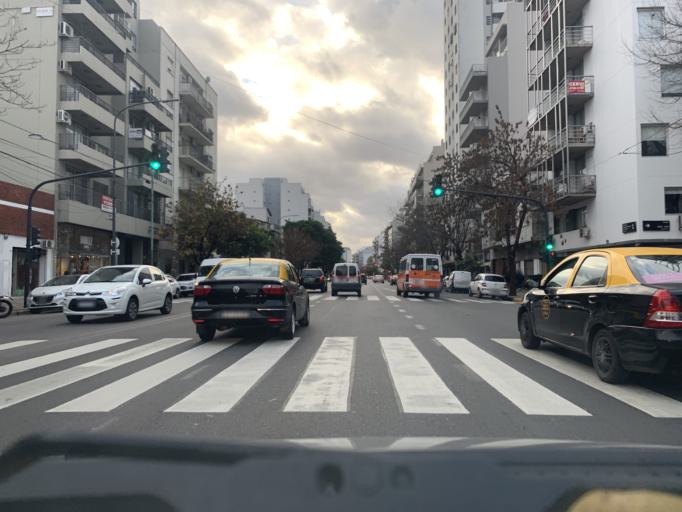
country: AR
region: Buenos Aires F.D.
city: Colegiales
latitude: -34.5799
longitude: -58.4528
